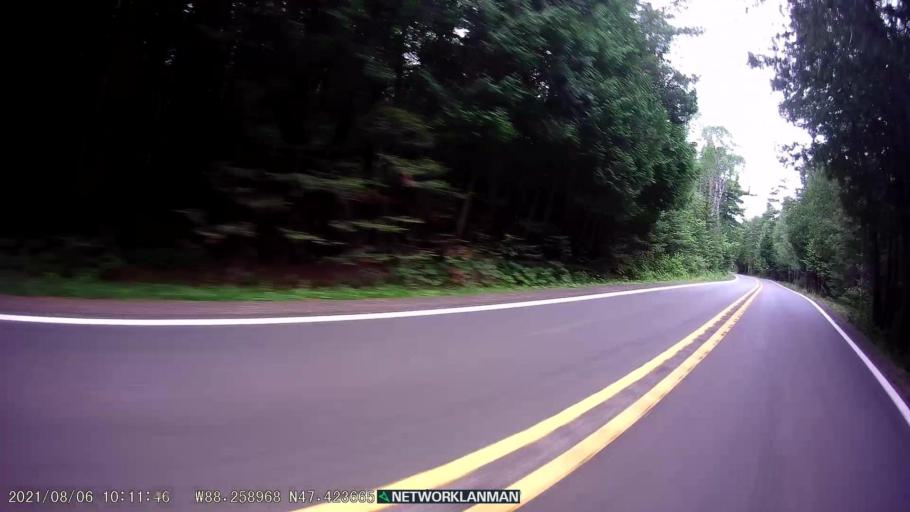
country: US
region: Michigan
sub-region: Keweenaw County
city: Eagle River
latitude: 47.4236
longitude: -88.2598
